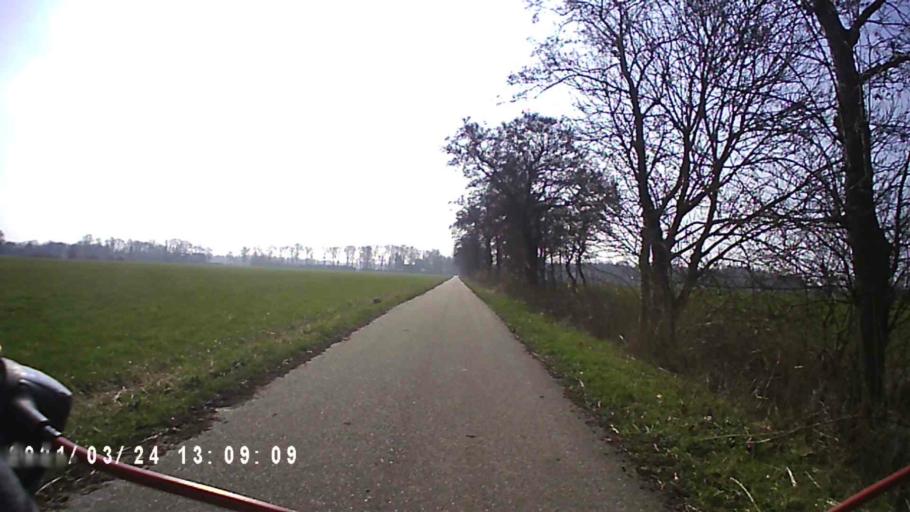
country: NL
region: Groningen
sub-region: Gemeente Leek
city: Leek
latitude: 53.1246
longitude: 6.3053
